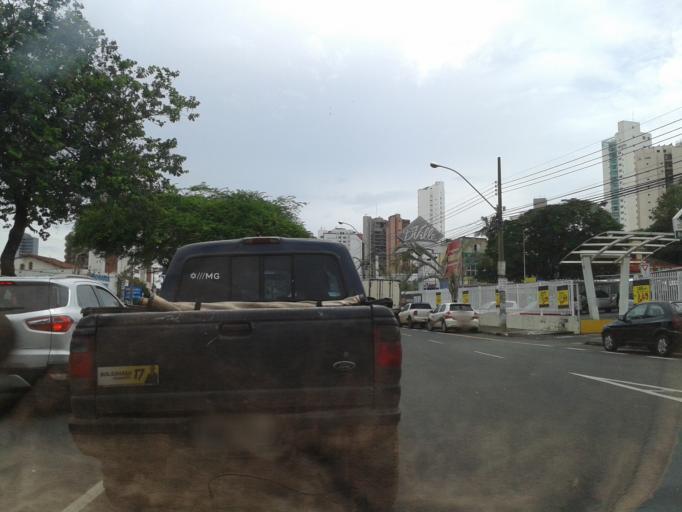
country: BR
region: Minas Gerais
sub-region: Uberlandia
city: Uberlandia
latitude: -18.9224
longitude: -48.2889
